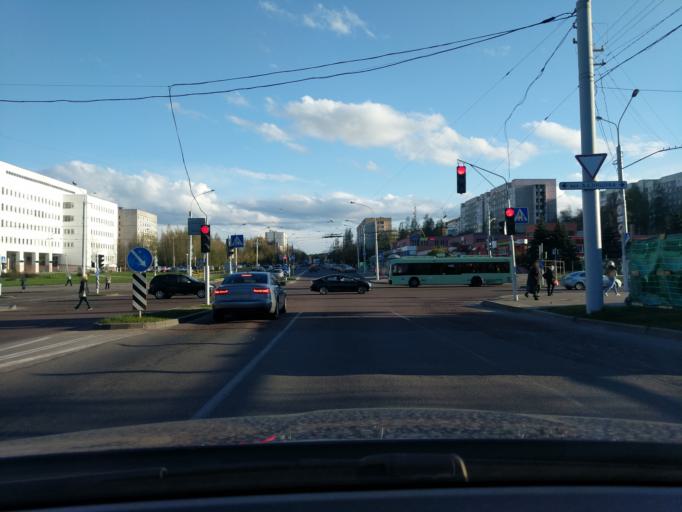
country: BY
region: Minsk
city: Novoye Medvezhino
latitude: 53.8992
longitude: 27.4529
